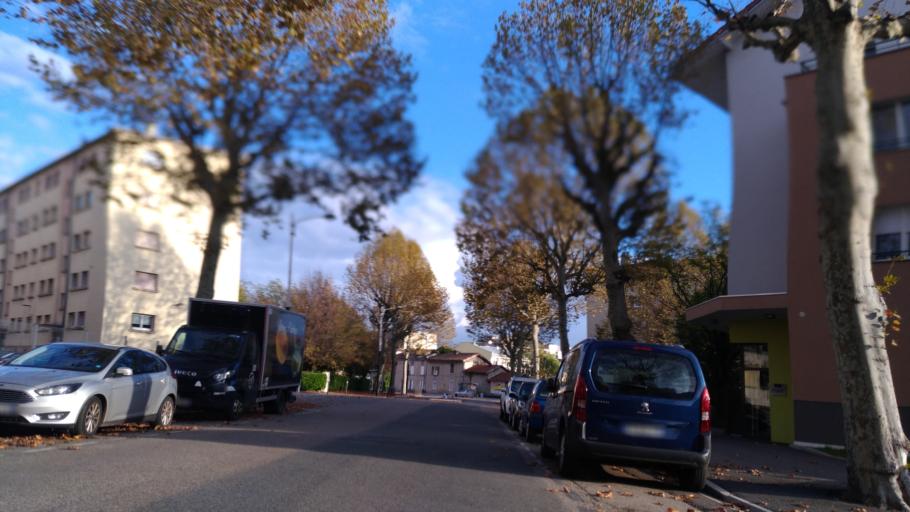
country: FR
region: Rhone-Alpes
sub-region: Departement de l'Isere
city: Fontaine
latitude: 45.1951
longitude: 5.6924
